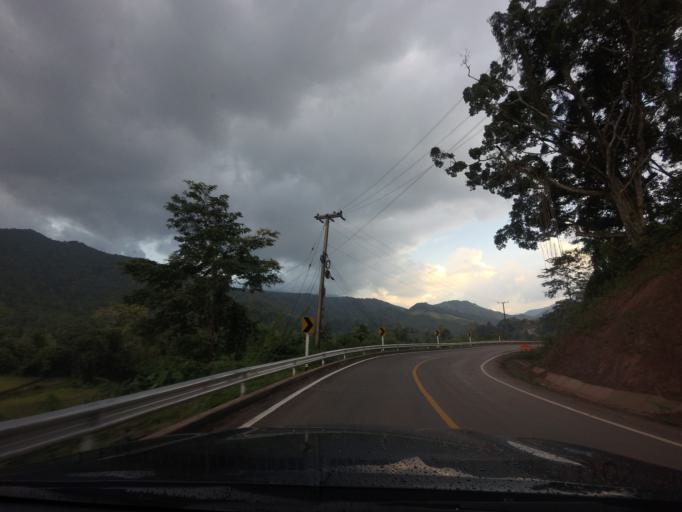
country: TH
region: Nan
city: Bo Kluea
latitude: 19.2218
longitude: 101.1830
